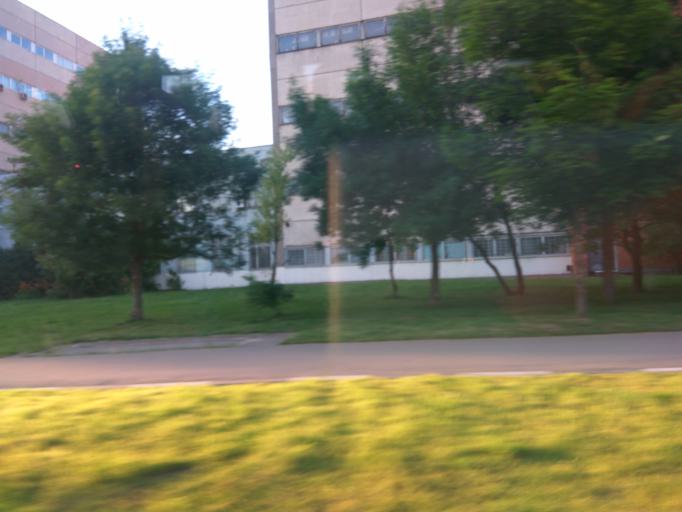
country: RU
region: Moscow
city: Chertanovo Yuzhnoye
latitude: 55.6132
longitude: 37.5859
